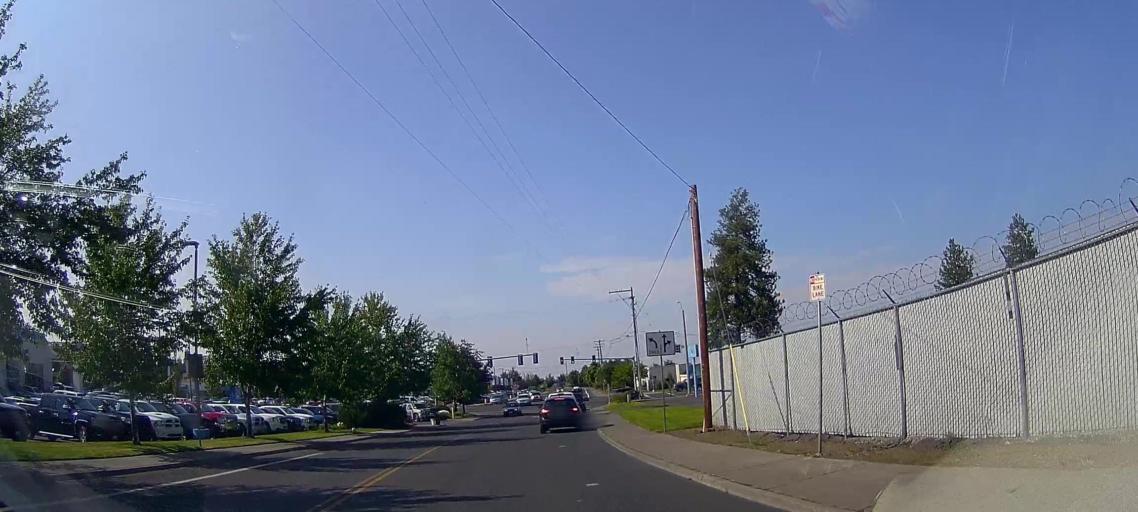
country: US
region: Oregon
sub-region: Deschutes County
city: Bend
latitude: 44.0542
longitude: -121.2686
